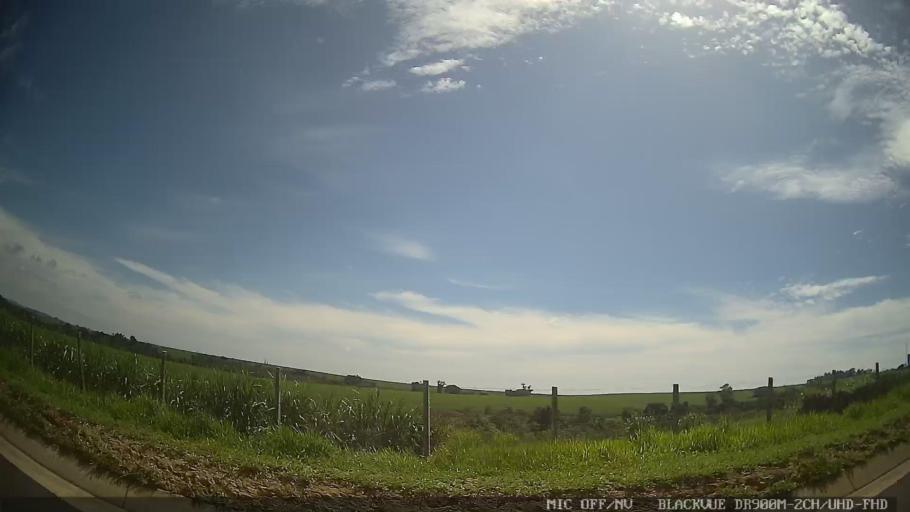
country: BR
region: Sao Paulo
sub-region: Tiete
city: Tiete
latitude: -23.1506
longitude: -47.6640
